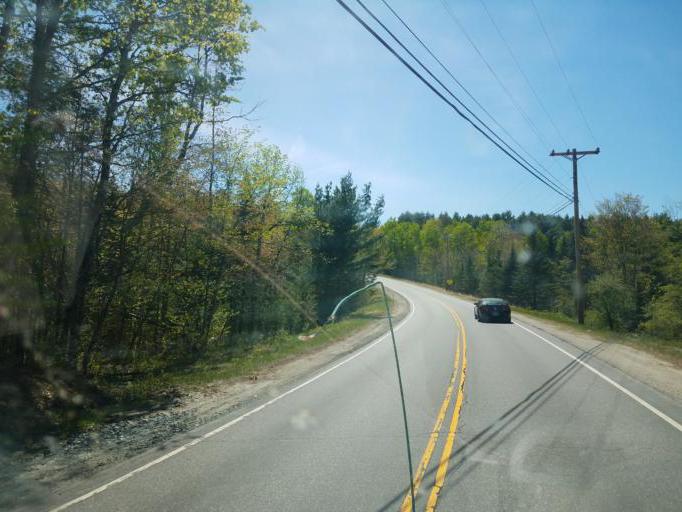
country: US
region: New Hampshire
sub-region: Grafton County
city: Rumney
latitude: 43.7986
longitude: -71.9126
